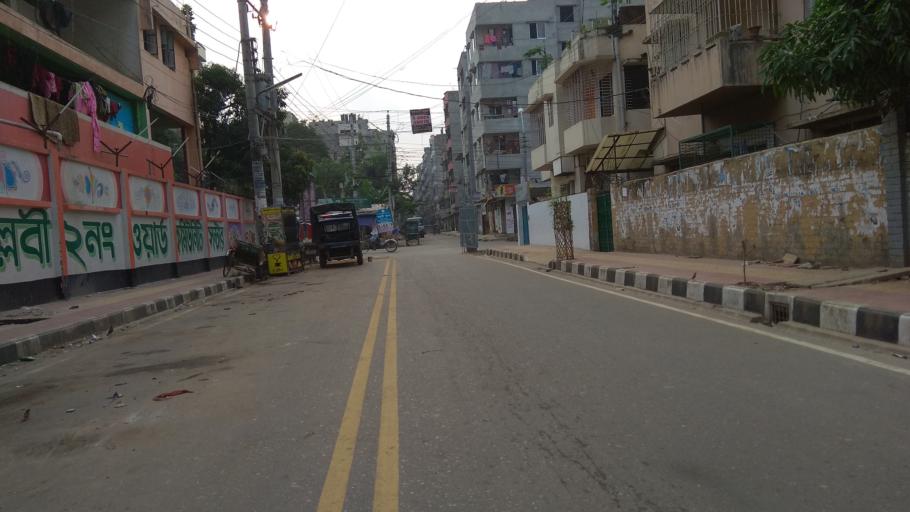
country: BD
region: Dhaka
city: Tungi
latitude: 23.8254
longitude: 90.3658
